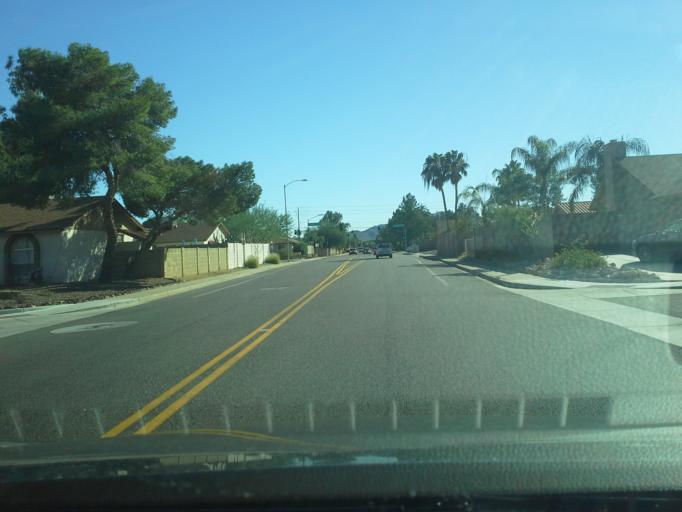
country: US
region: Arizona
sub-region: Maricopa County
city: Paradise Valley
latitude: 33.6131
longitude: -111.9866
